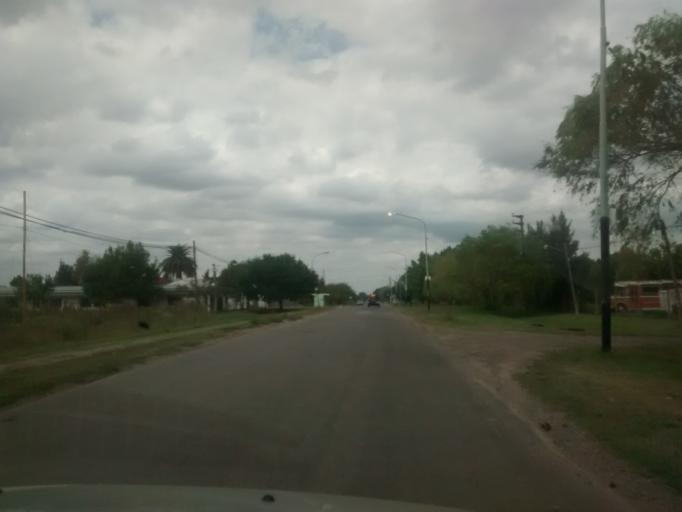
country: AR
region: Buenos Aires
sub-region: Partido de La Plata
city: La Plata
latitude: -34.9692
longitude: -57.9463
